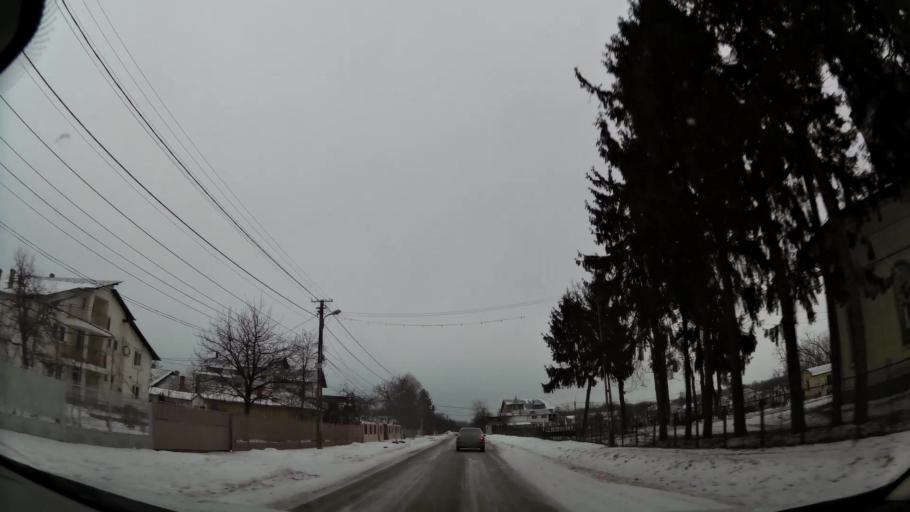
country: RO
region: Prahova
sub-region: Comuna Poenarii-Burchi
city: Ologeni
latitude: 44.7276
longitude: 25.9592
